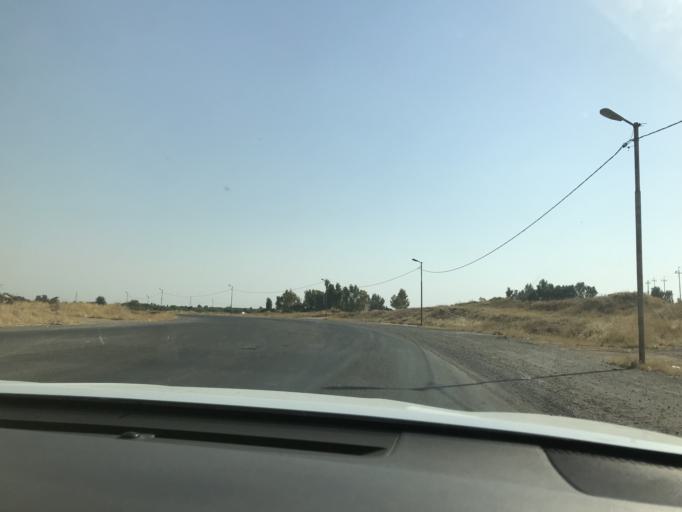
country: IQ
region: Arbil
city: Erbil
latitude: 36.1737
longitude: 43.9244
